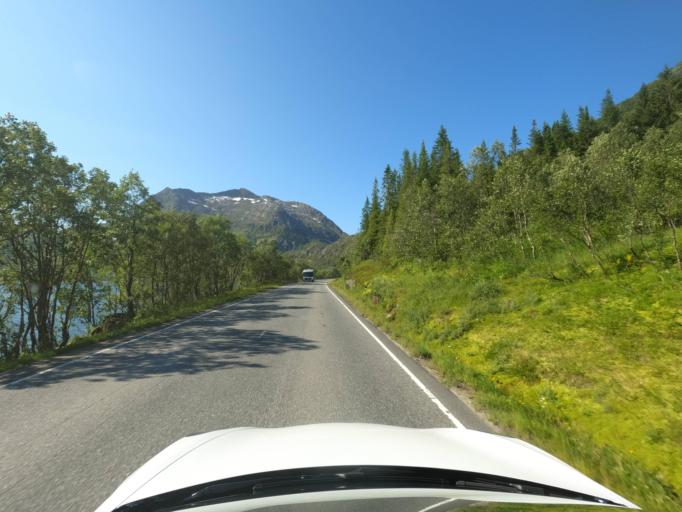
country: NO
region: Nordland
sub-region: Lodingen
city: Lodingen
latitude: 68.5446
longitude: 15.7377
